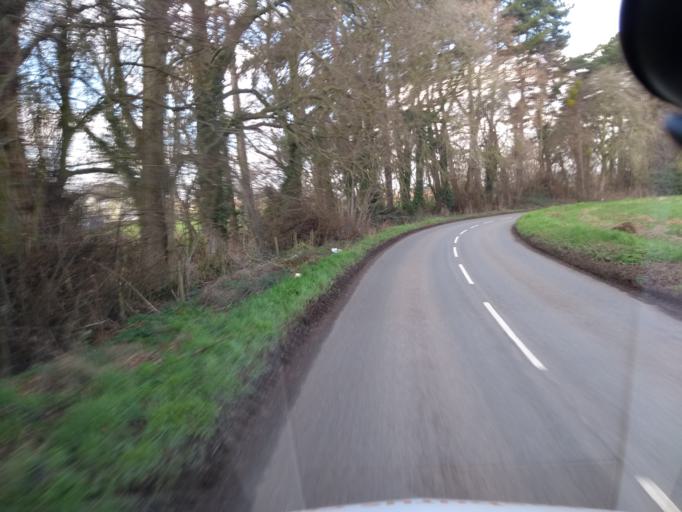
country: GB
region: England
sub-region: Somerset
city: Taunton
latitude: 50.9905
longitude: -3.0736
